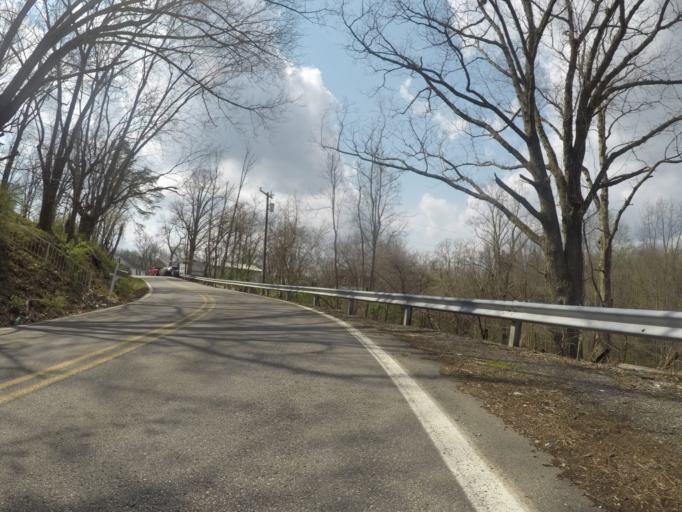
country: US
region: West Virginia
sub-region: Cabell County
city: Pea Ridge
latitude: 38.3457
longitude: -82.3611
